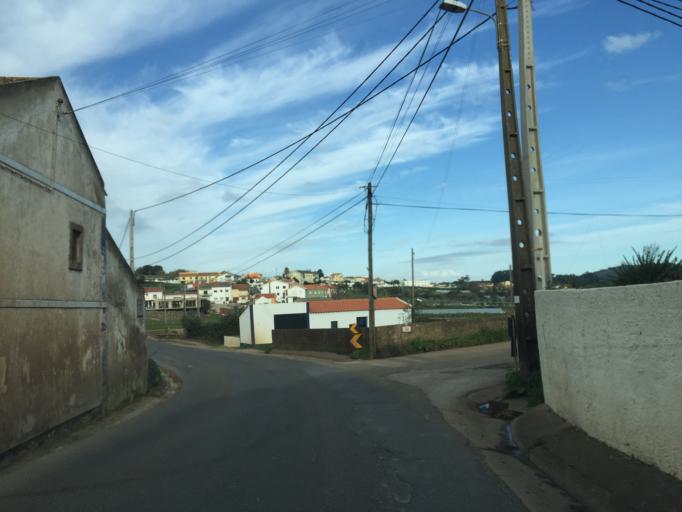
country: PT
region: Lisbon
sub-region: Sintra
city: Almargem
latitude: 38.8337
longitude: -9.2514
